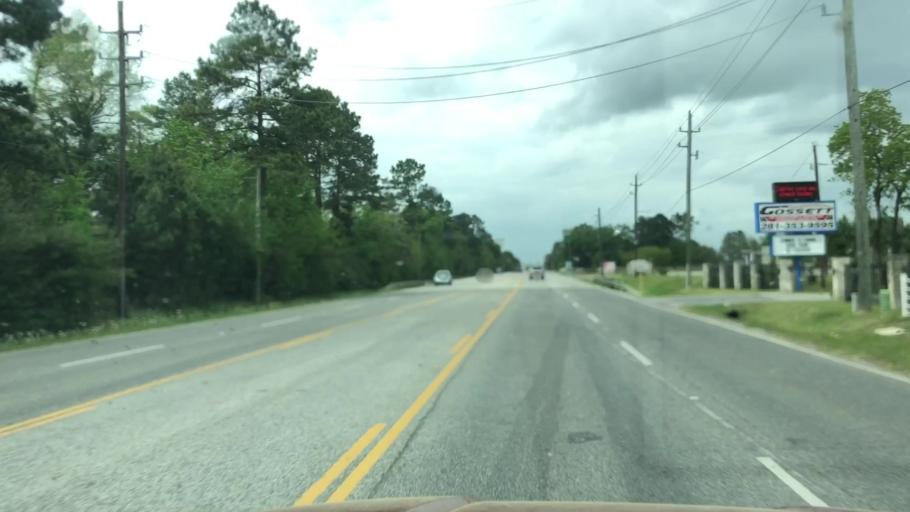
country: US
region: Texas
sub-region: Harris County
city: Spring
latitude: 30.0618
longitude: -95.4991
